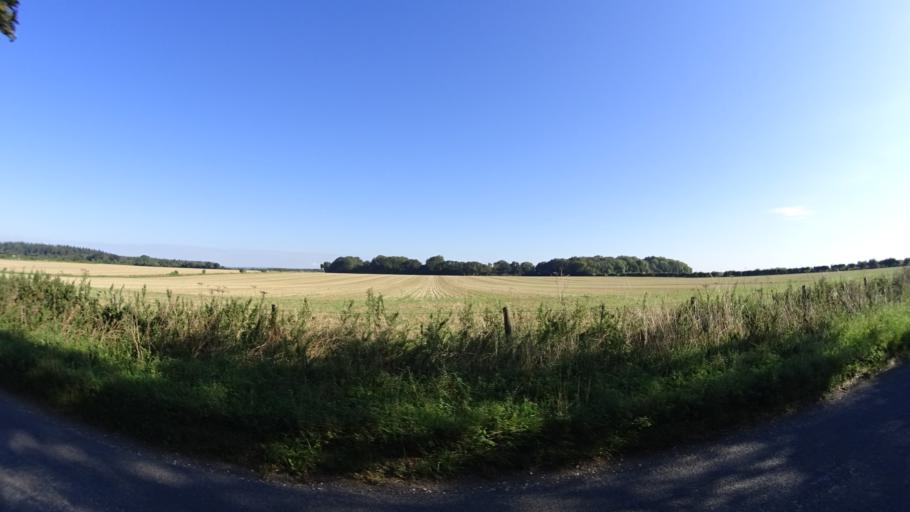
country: GB
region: England
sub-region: Hampshire
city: Abbotts Ann
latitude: 51.1615
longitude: -1.5718
